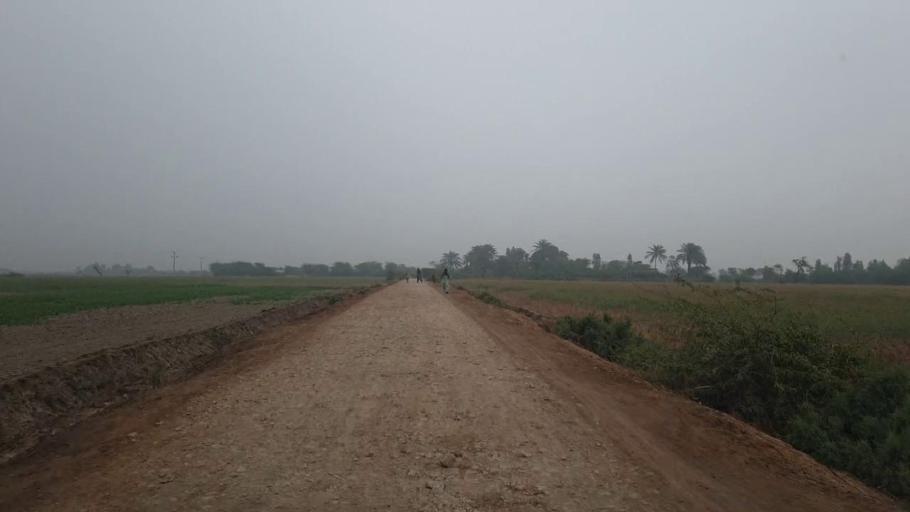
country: PK
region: Sindh
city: Badin
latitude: 24.6262
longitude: 68.7002
